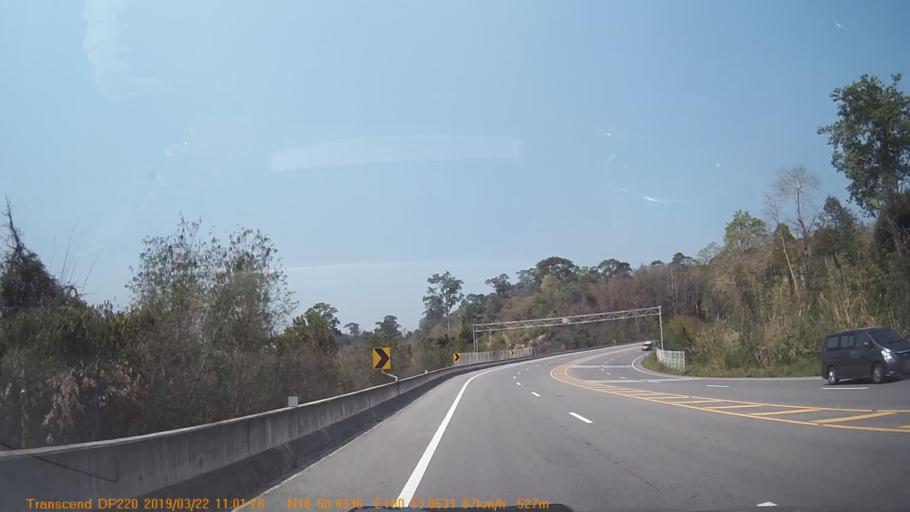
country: TH
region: Phetchabun
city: Khao Kho
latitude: 16.8404
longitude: 100.8839
